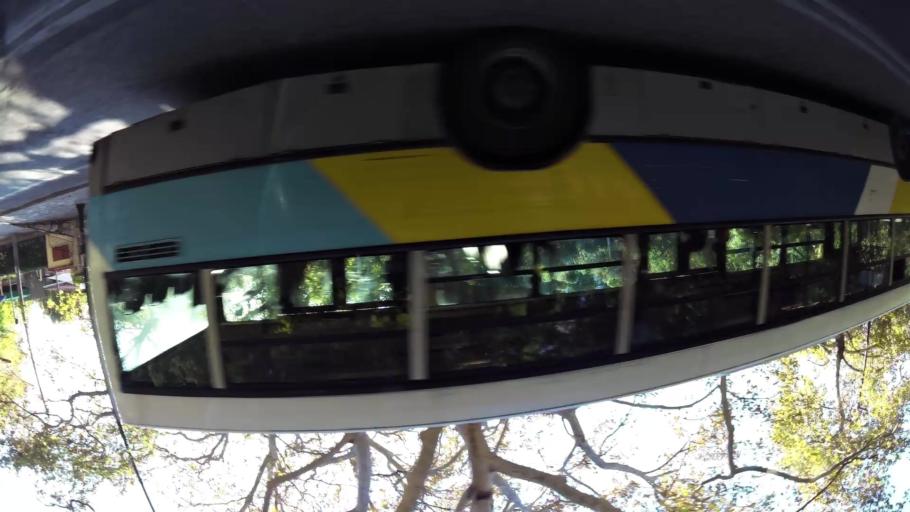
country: GR
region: Attica
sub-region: Nomarchia Athinas
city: Penteli
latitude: 38.0523
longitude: 23.8657
